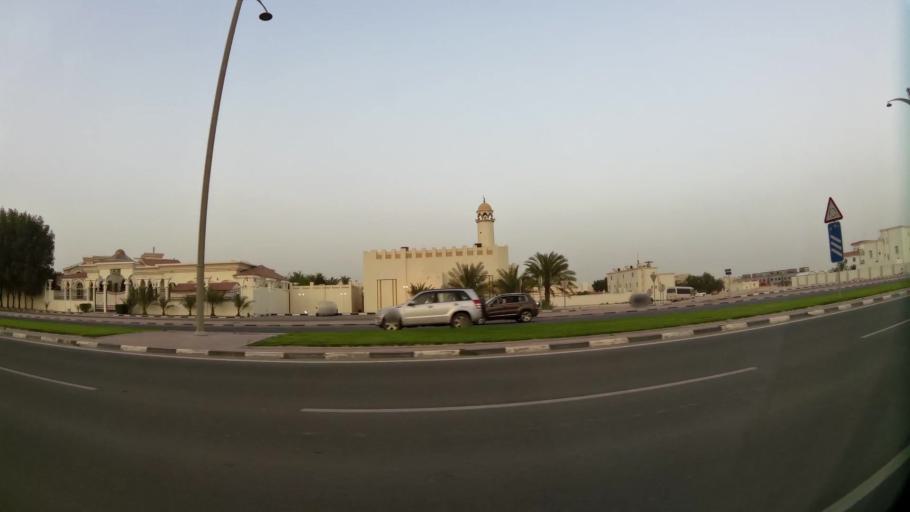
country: QA
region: Baladiyat ar Rayyan
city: Ar Rayyan
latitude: 25.2627
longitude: 51.4648
